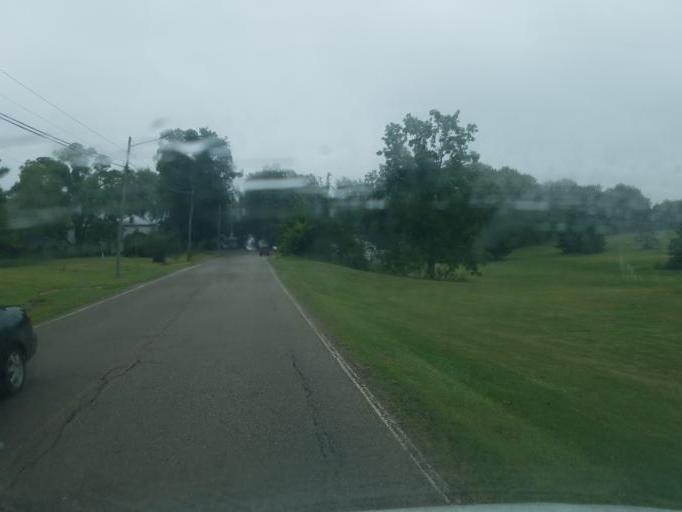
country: US
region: Ohio
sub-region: Knox County
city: Centerburg
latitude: 40.2354
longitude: -82.6880
